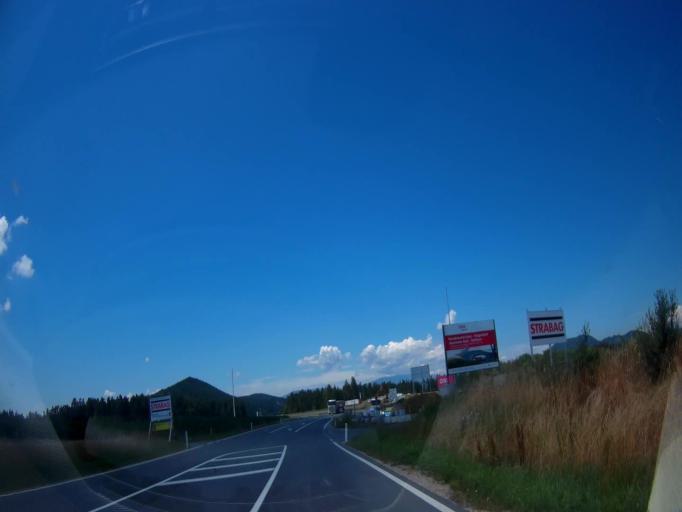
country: AT
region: Carinthia
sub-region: Politischer Bezirk Volkermarkt
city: Bleiburg/Pliberk
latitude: 46.6068
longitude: 14.7840
